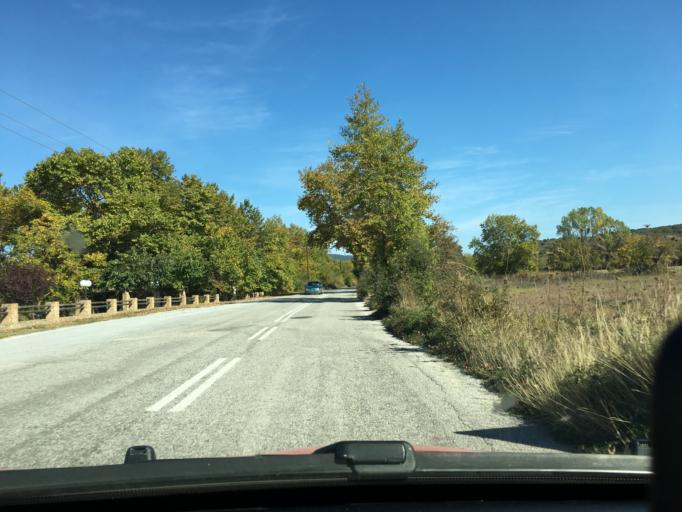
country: GR
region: Central Macedonia
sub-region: Nomos Chalkidikis
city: Megali Panagia
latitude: 40.3781
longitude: 23.6969
